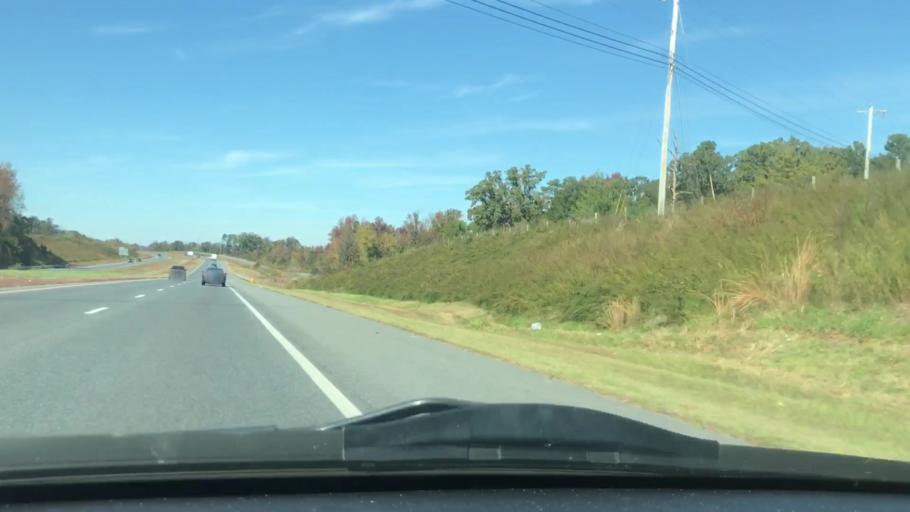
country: US
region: North Carolina
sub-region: Randolph County
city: Randleman
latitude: 35.8356
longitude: -79.8611
